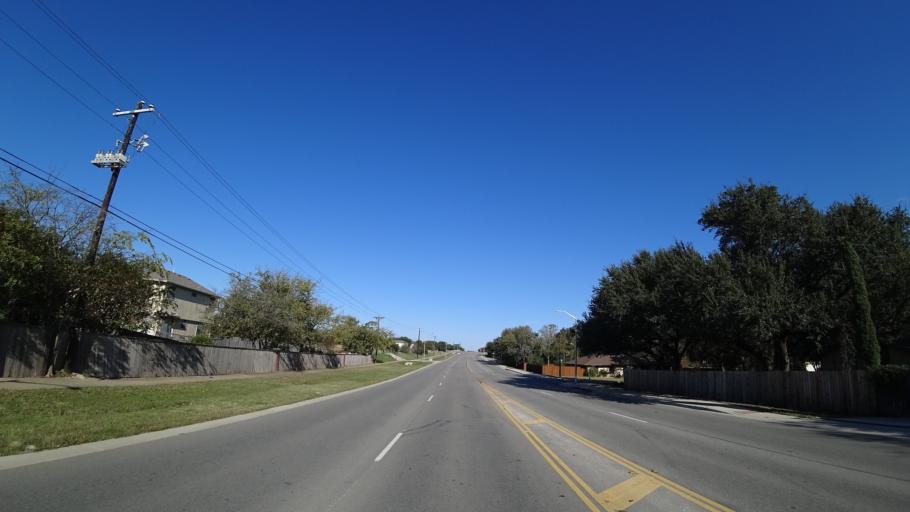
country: US
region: Texas
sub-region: Williamson County
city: Cedar Park
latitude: 30.5208
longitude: -97.8414
